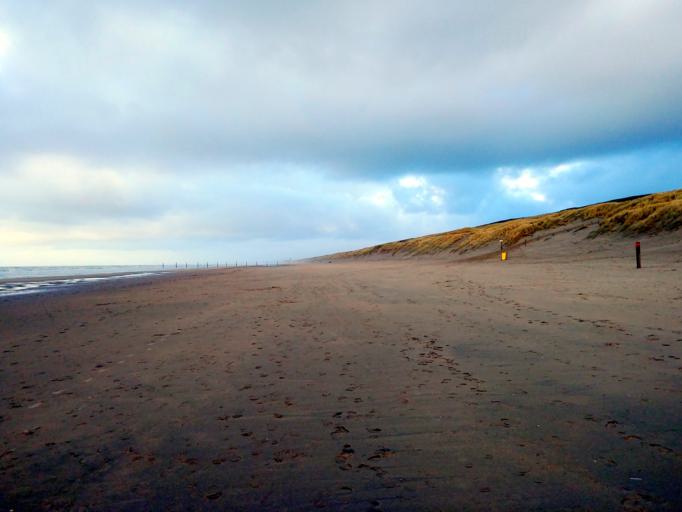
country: NL
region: South Holland
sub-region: Gemeente Noordwijkerhout
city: Noordwijkerhout
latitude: 52.3117
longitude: 4.4817
